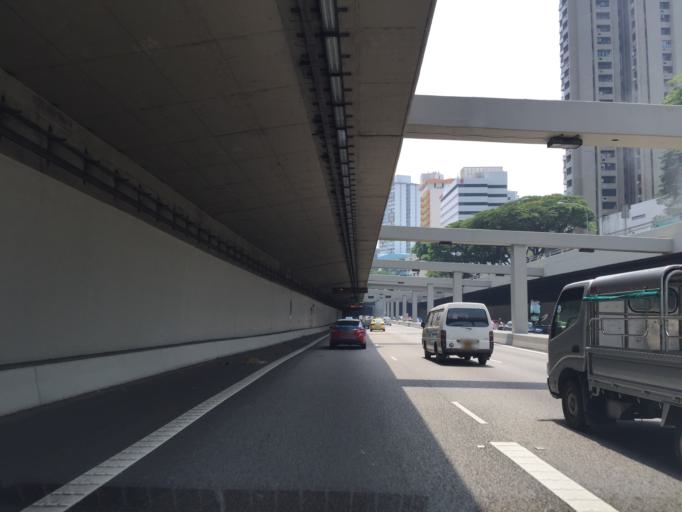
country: SG
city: Singapore
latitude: 1.2860
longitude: 103.8381
